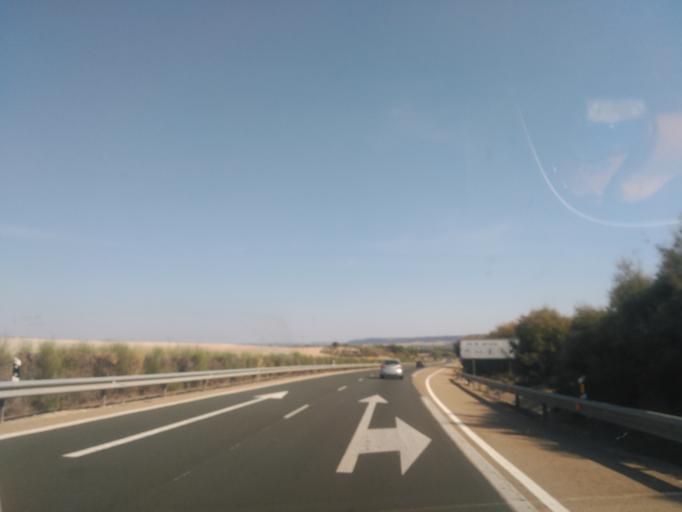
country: ES
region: Castille and Leon
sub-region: Provincia de Valladolid
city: Tudela de Duero
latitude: 41.5963
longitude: -4.6271
